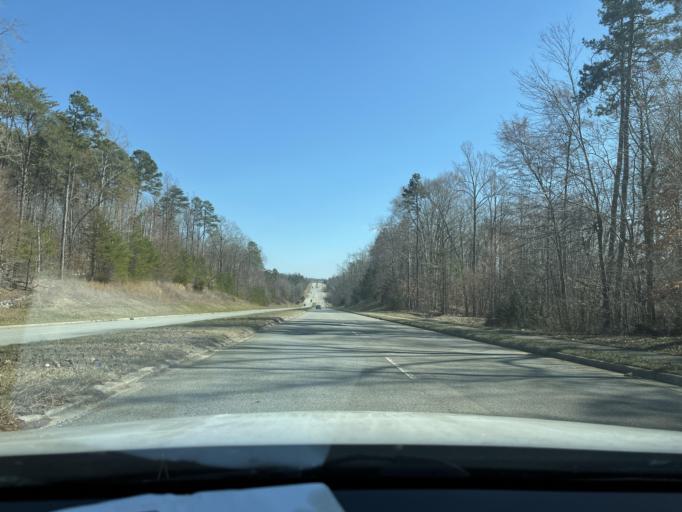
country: US
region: North Carolina
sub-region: Guilford County
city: Jamestown
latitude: 36.0103
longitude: -79.9252
